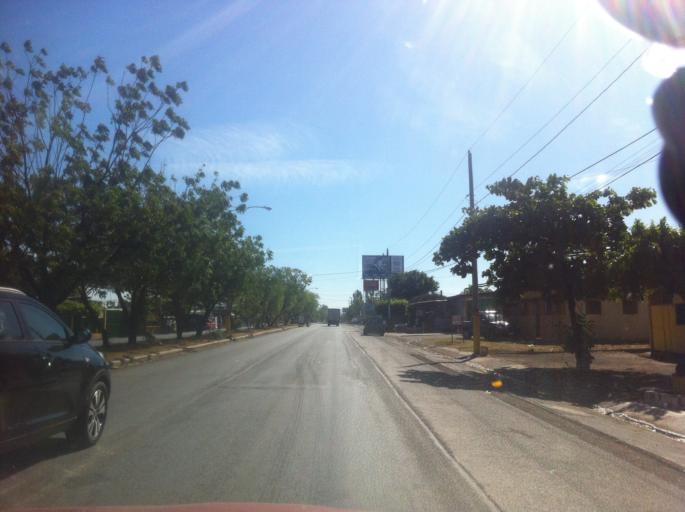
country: NI
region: Managua
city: Tipitapa
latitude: 12.1976
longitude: -86.1037
